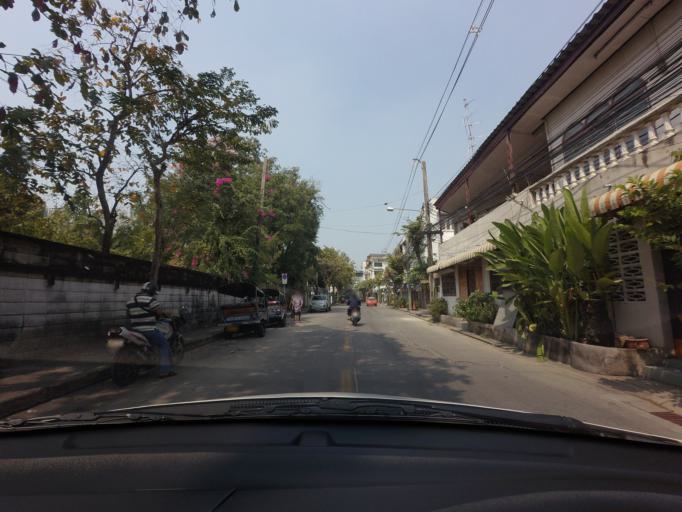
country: TH
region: Bangkok
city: Bangkok Noi
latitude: 13.7629
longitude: 100.4747
